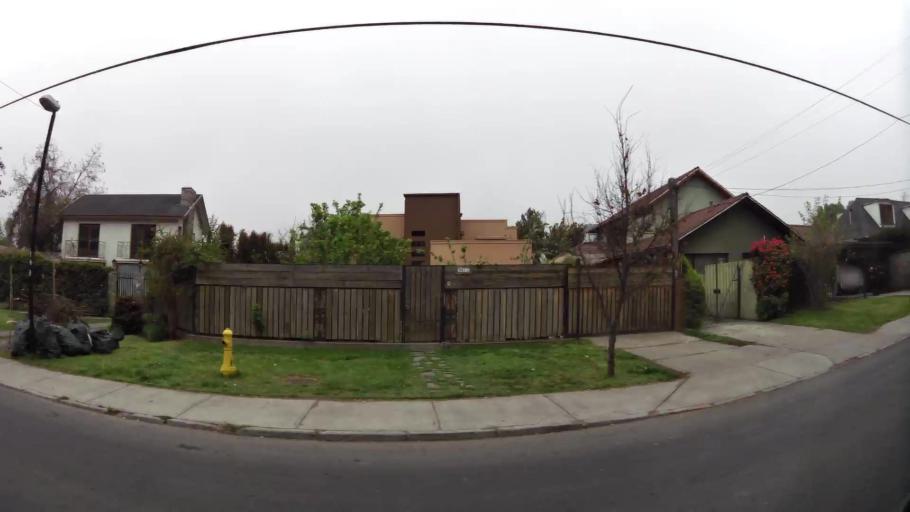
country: CL
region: Santiago Metropolitan
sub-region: Provincia de Santiago
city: Villa Presidente Frei, Nunoa, Santiago, Chile
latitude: -33.3998
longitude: -70.5825
